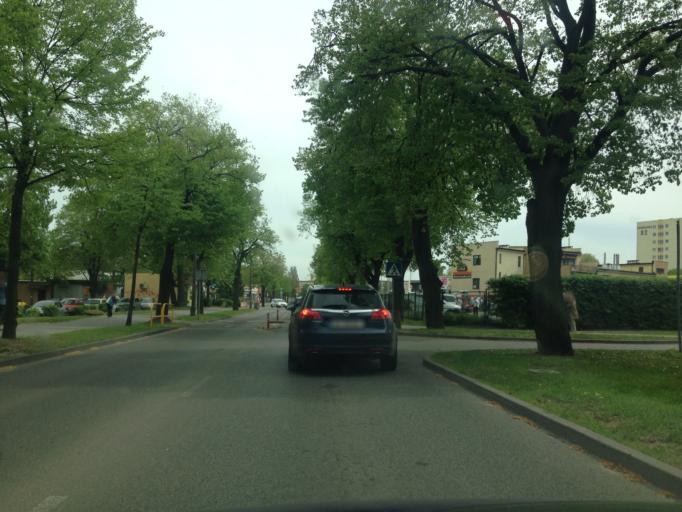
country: PL
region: Pomeranian Voivodeship
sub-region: Sopot
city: Sopot
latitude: 54.4216
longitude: 18.5811
